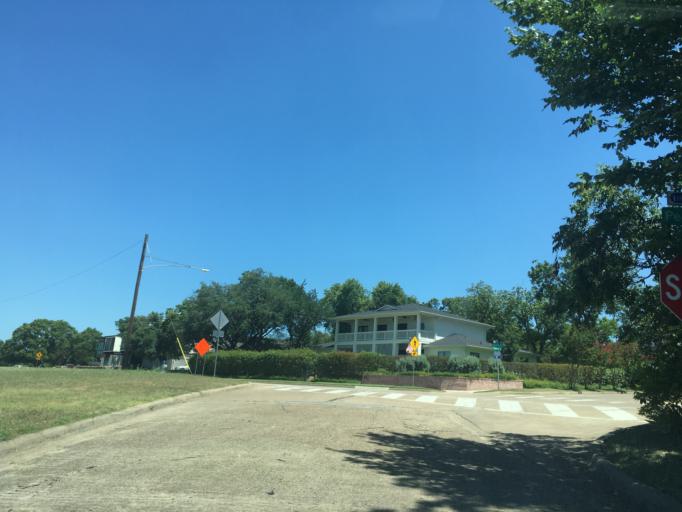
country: US
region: Texas
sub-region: Dallas County
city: Highland Park
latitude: 32.8514
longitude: -96.7148
